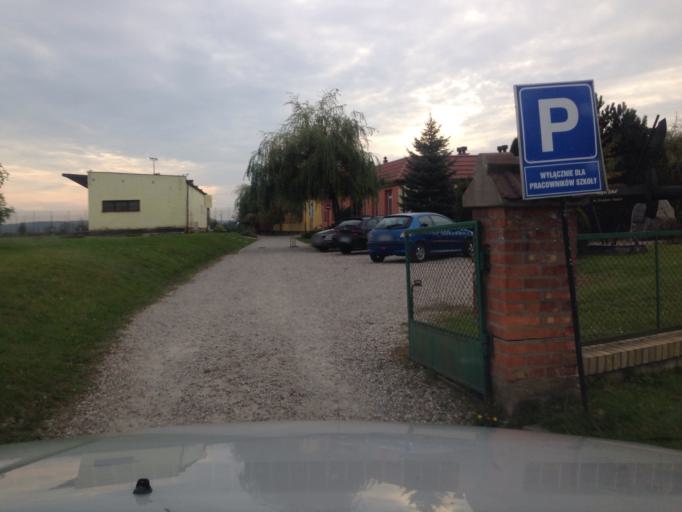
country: PL
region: Pomeranian Voivodeship
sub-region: Powiat leborski
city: Nowa Wies Leborska
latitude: 54.5604
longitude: 17.7385
